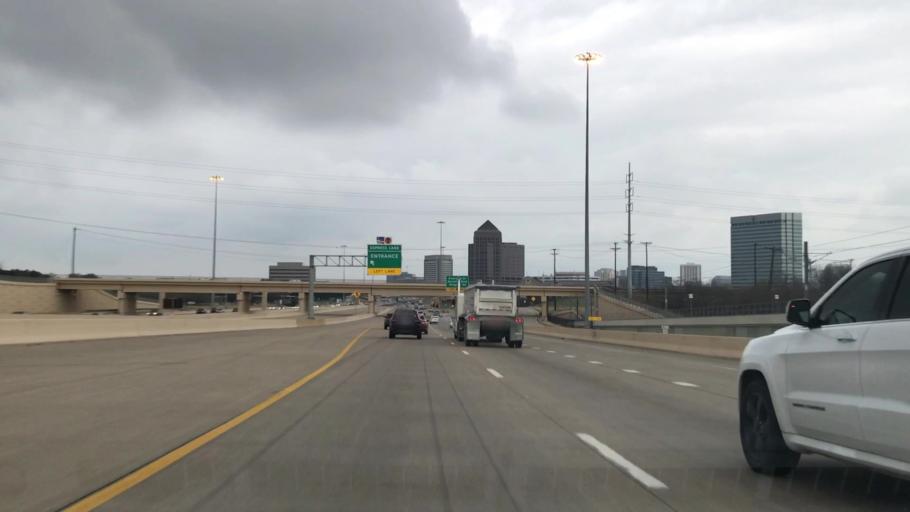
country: US
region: Texas
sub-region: Dallas County
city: Irving
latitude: 32.8537
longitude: -96.9244
